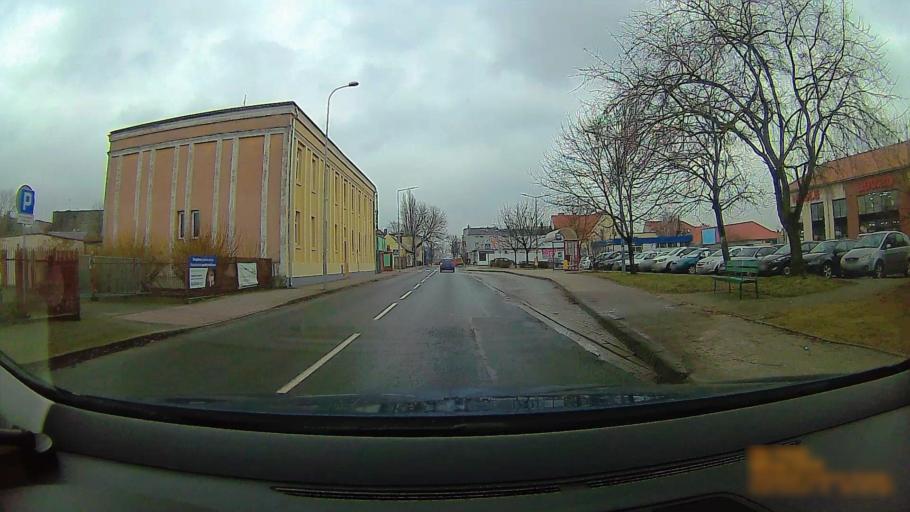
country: PL
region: Greater Poland Voivodeship
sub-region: Konin
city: Konin
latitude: 52.2089
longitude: 18.2521
